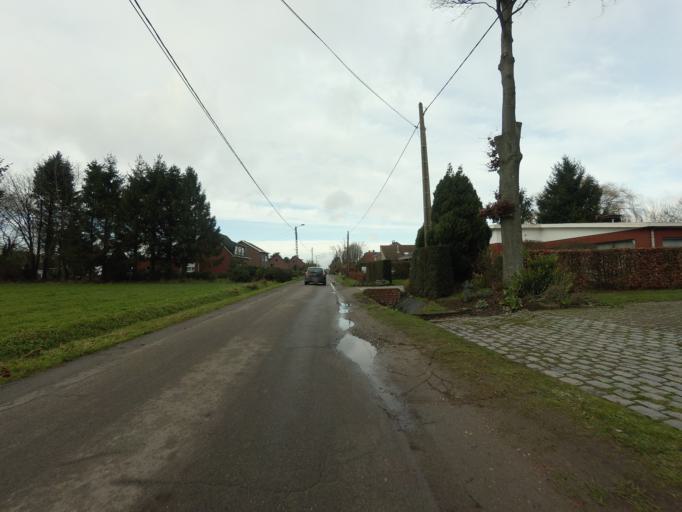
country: BE
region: Flanders
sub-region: Provincie Antwerpen
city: Sint-Katelijne-Waver
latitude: 51.0868
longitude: 4.5392
